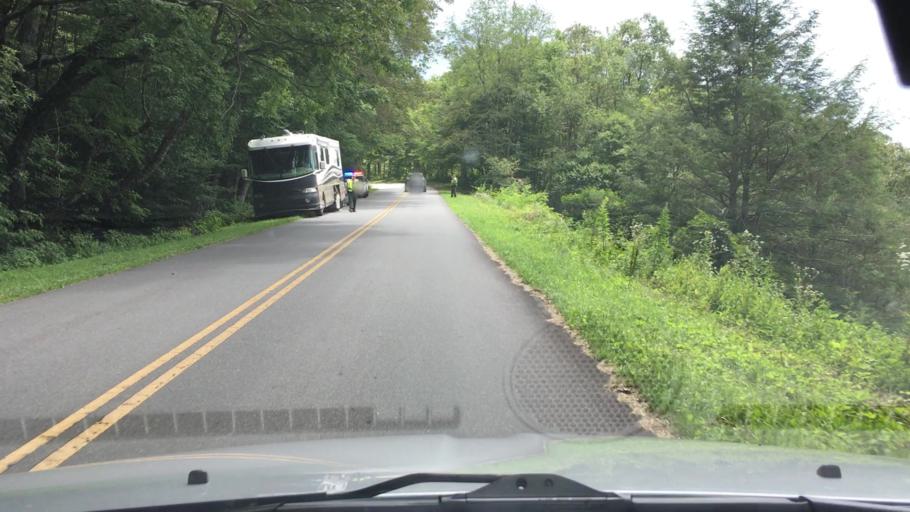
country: US
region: North Carolina
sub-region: Buncombe County
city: Swannanoa
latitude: 35.6776
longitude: -82.4256
